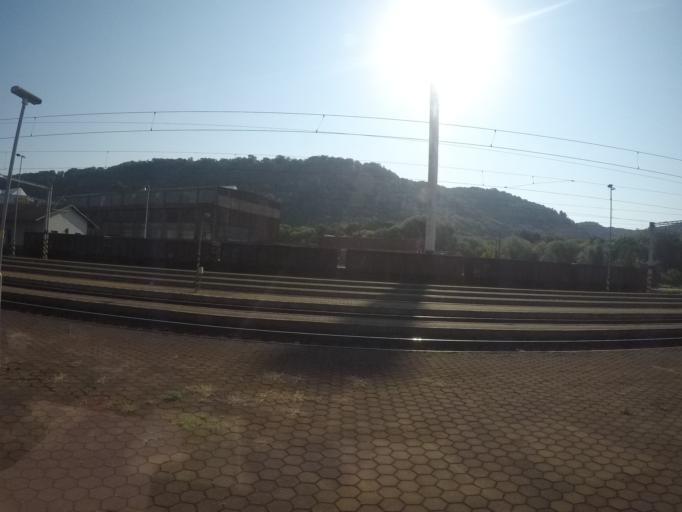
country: SK
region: Kosicky
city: Kosice
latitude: 48.8512
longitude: 21.2242
